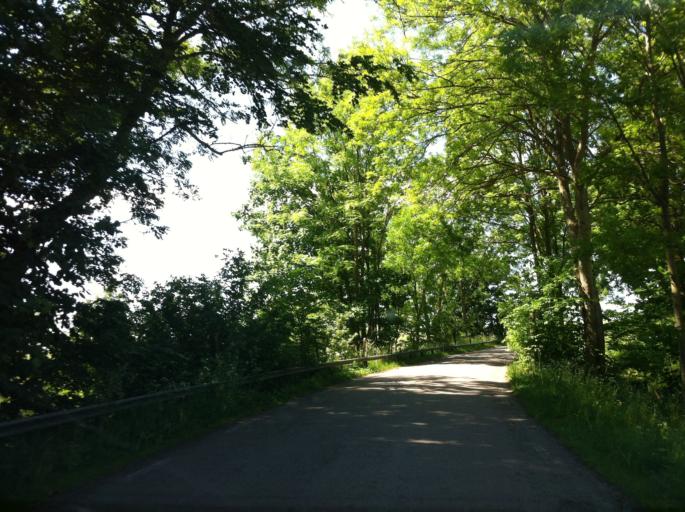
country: SE
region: Skane
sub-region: Landskrona
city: Asmundtorp
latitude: 55.9426
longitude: 12.9158
